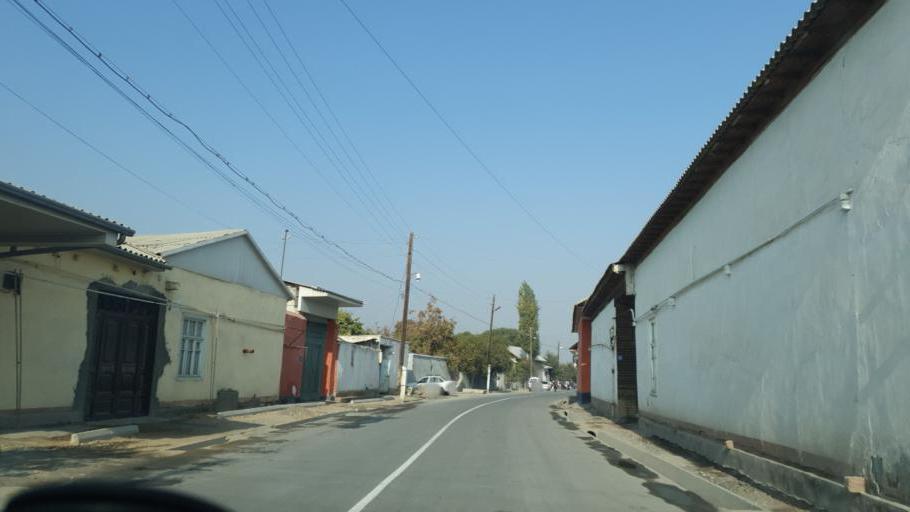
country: UZ
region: Fergana
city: Qo`qon
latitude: 40.5834
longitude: 70.9091
